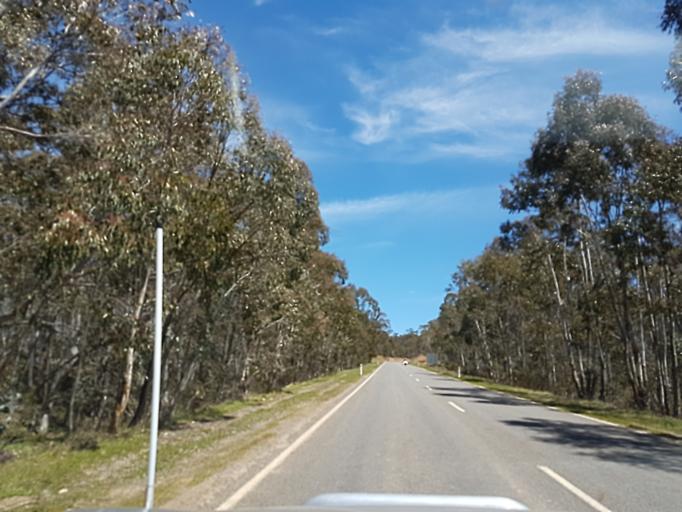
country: AU
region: Victoria
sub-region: Alpine
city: Mount Beauty
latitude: -37.0927
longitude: 147.3856
